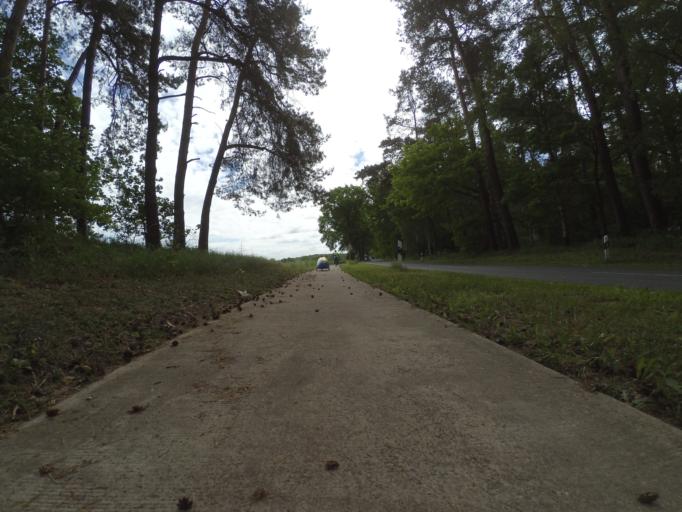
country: DE
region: Lower Saxony
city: Garbsen
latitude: 52.4249
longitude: 9.5339
